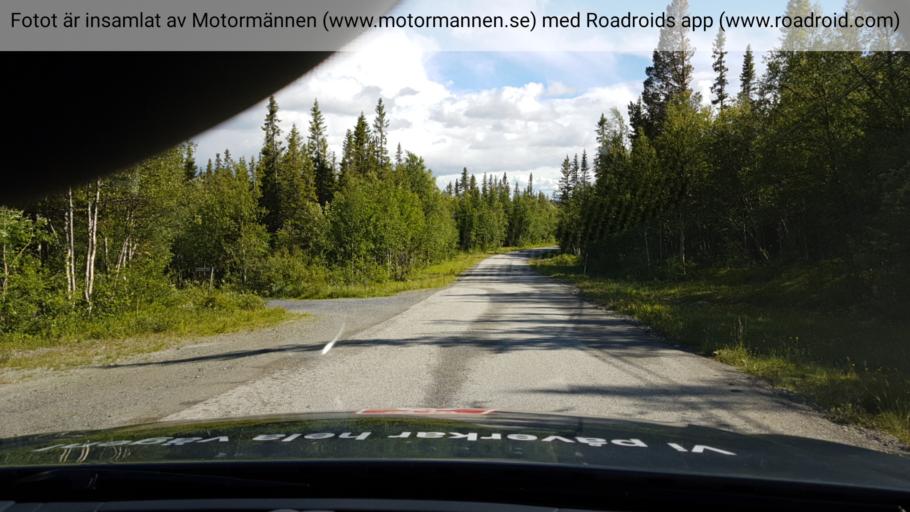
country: SE
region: Jaemtland
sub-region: Krokoms Kommun
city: Valla
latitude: 63.0254
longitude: 13.9449
